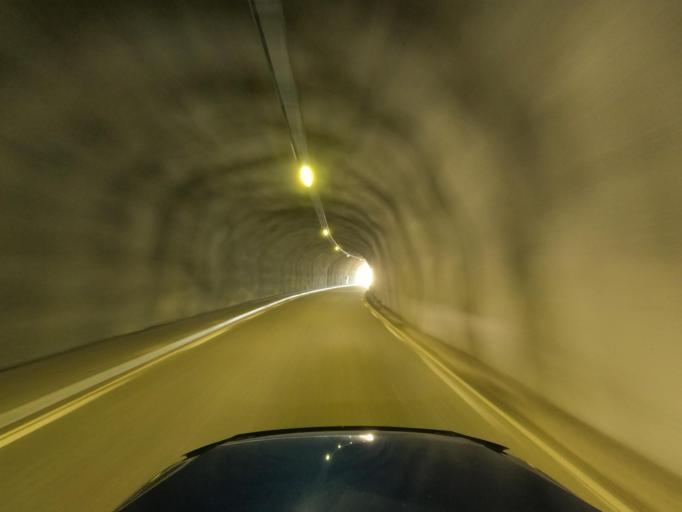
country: NO
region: Nordland
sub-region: Moskenes
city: Reine
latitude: 67.8814
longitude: 12.9795
